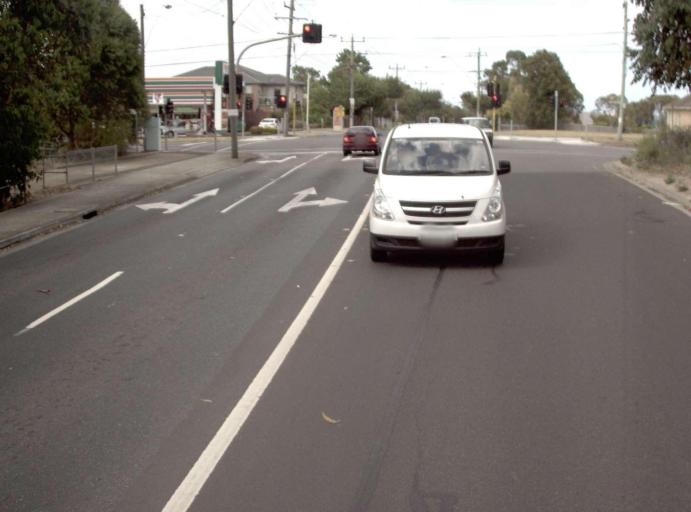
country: AU
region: Victoria
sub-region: Monash
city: Oakleigh South
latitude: -37.9257
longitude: 145.1007
